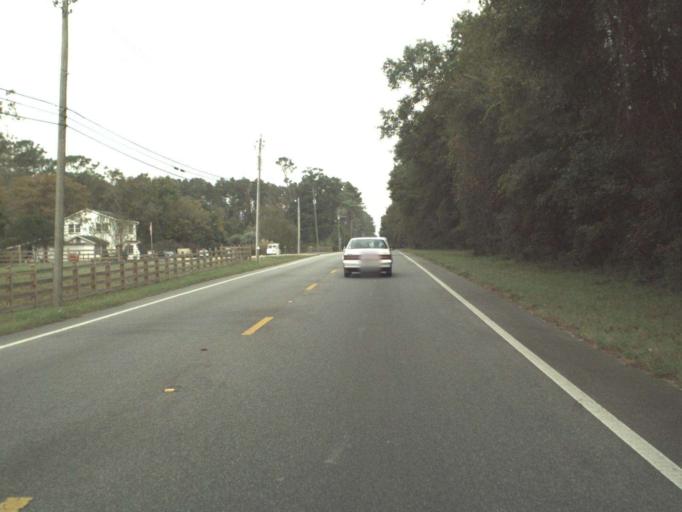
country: US
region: Florida
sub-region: Leon County
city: Woodville
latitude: 30.2931
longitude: -84.2430
